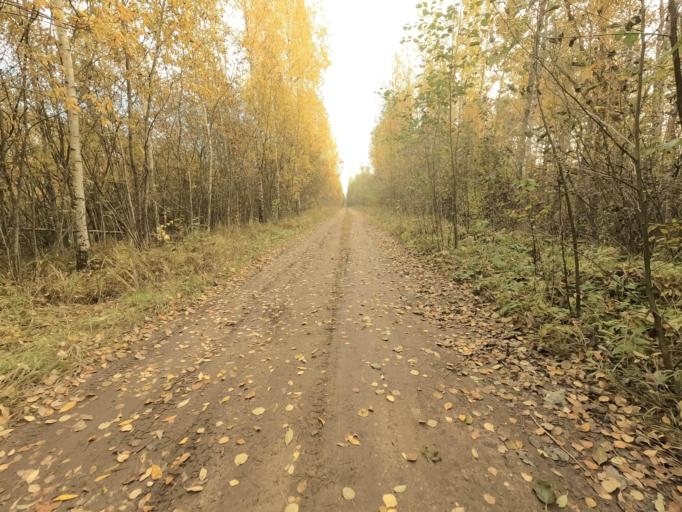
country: RU
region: Novgorod
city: Pankovka
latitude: 58.8787
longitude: 30.8569
